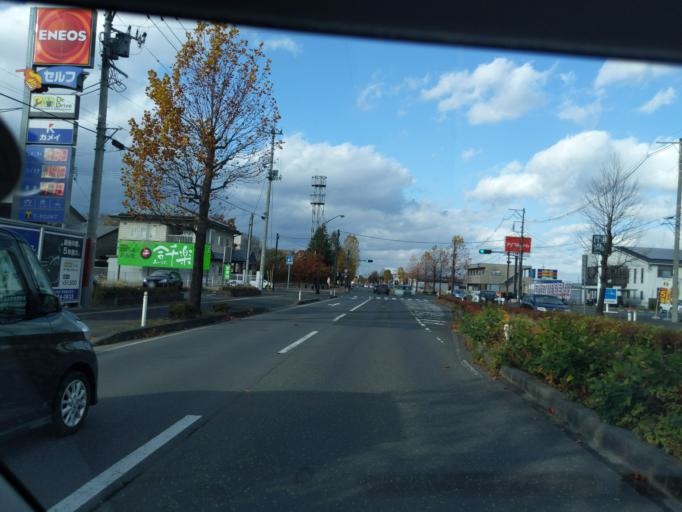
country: JP
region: Iwate
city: Mizusawa
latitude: 39.1437
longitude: 141.1550
